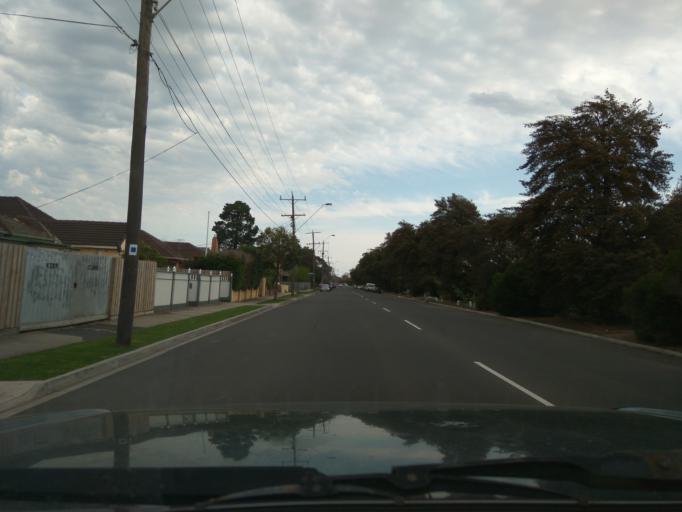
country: AU
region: Victoria
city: Spotswood
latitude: -37.8324
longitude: 144.8858
